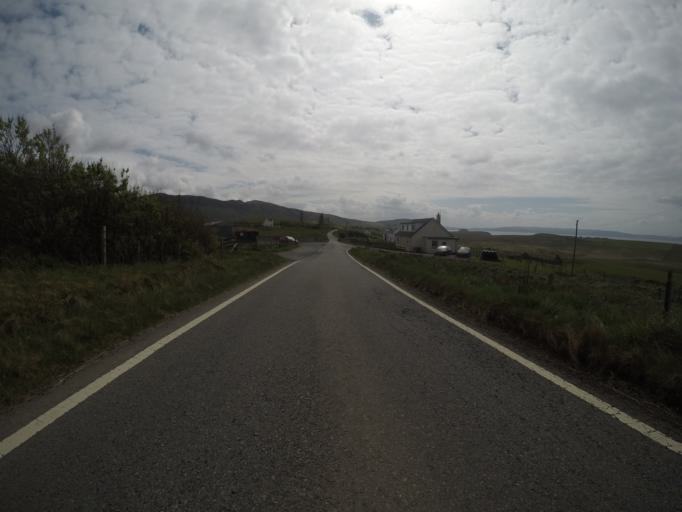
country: GB
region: Scotland
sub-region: Highland
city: Portree
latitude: 57.6292
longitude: -6.3782
